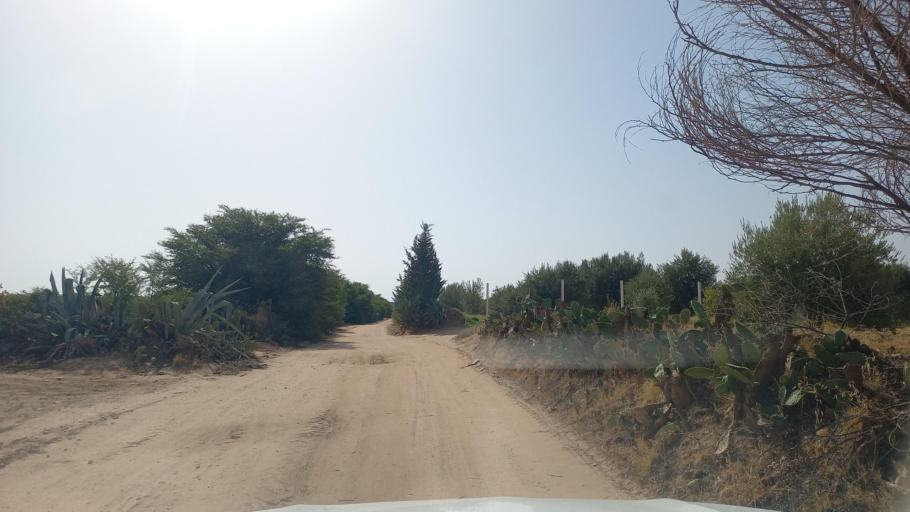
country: TN
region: Al Qasrayn
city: Kasserine
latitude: 35.2492
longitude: 9.0333
